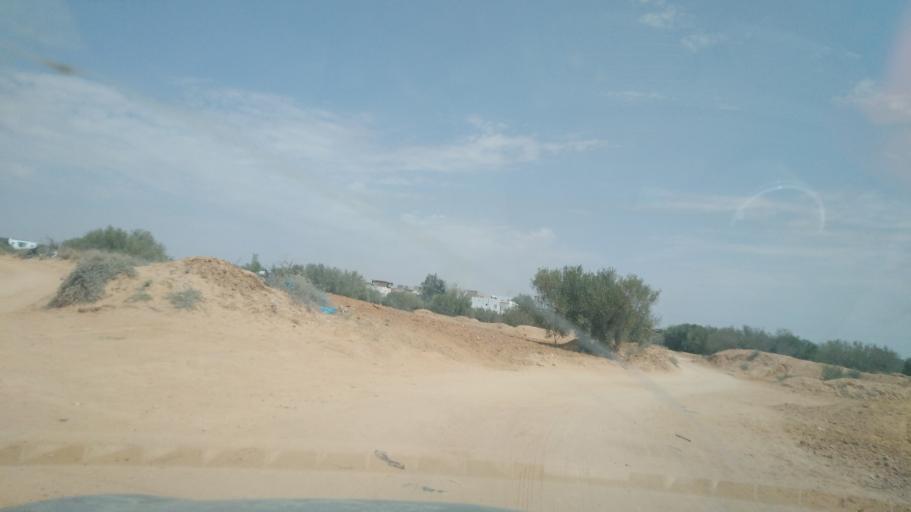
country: TN
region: Safaqis
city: Sfax
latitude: 34.7391
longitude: 10.5596
